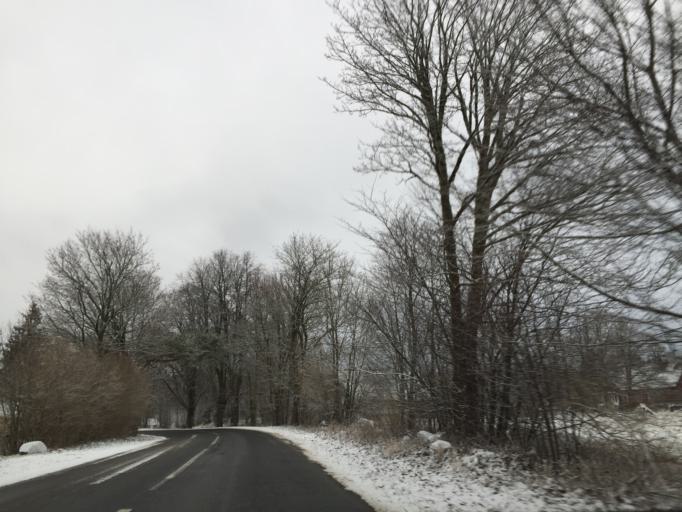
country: EE
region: Saare
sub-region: Orissaare vald
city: Orissaare
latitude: 58.6110
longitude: 23.2997
